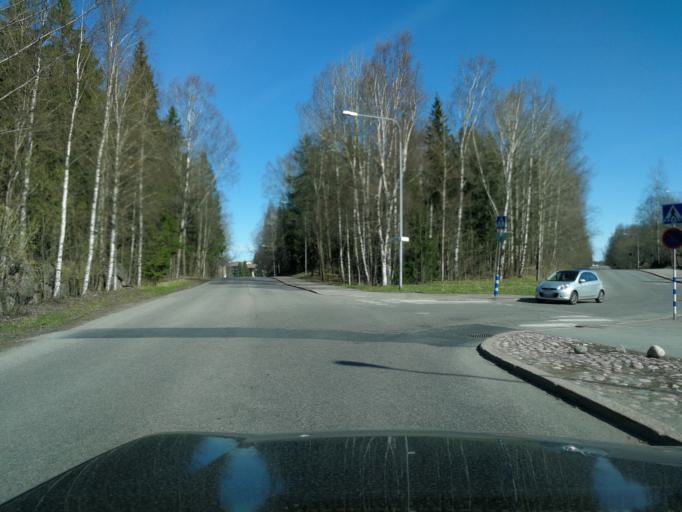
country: FI
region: Uusimaa
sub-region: Helsinki
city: Helsinki
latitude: 60.2231
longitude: 24.9336
